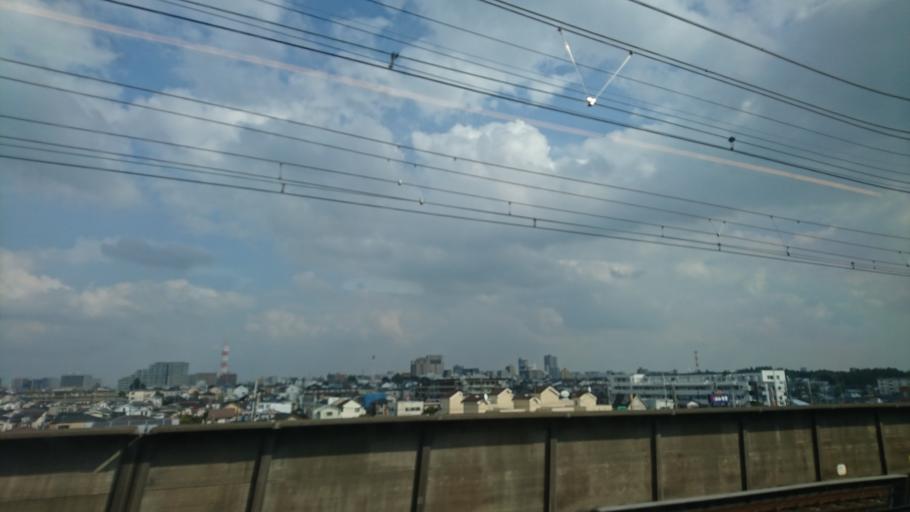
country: JP
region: Saitama
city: Yono
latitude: 35.8624
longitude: 139.6330
